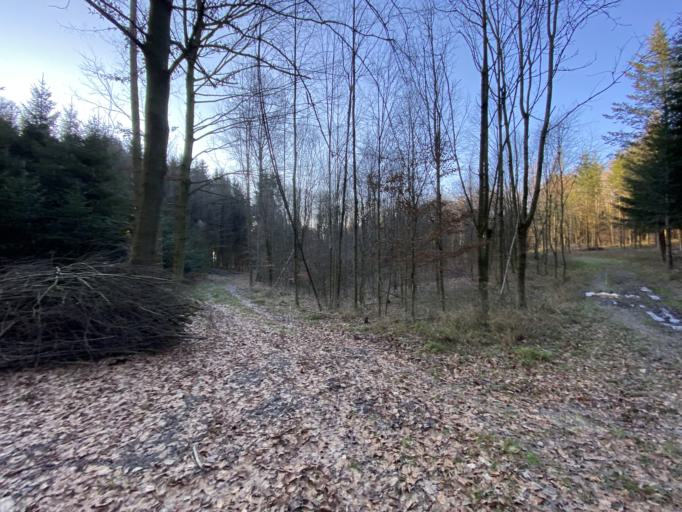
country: AT
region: Lower Austria
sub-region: Politischer Bezirk Sankt Polten
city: Boheimkirchen
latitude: 48.2085
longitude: 15.7241
